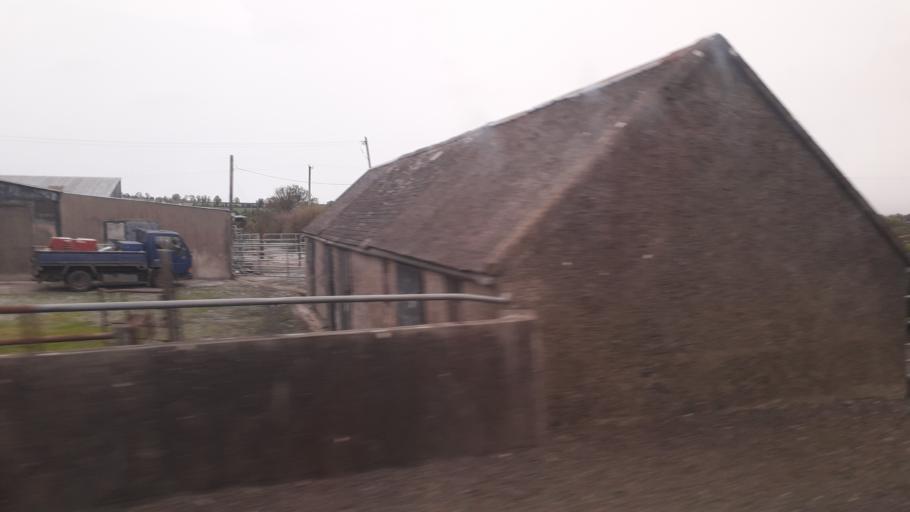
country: IE
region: Leinster
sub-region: Uibh Fhaili
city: Birr
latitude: 52.9745
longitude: -7.9829
